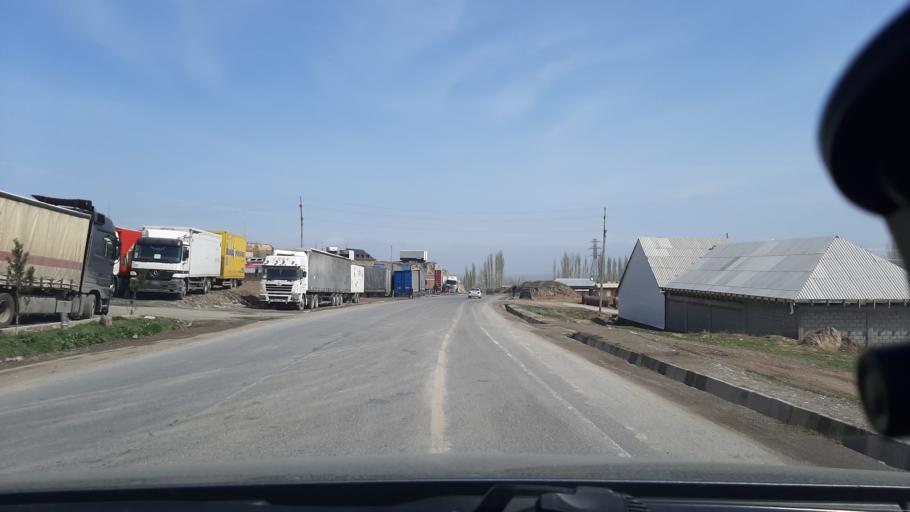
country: TJ
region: Viloyati Sughd
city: Istaravshan
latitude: 39.8640
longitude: 68.9894
